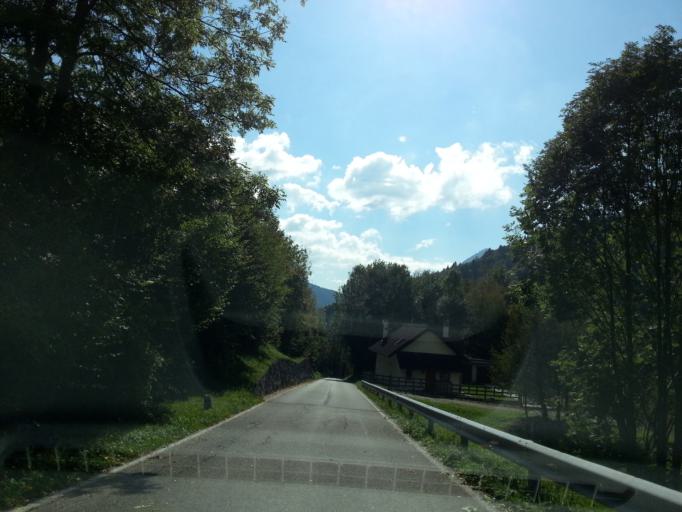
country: IT
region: Friuli Venezia Giulia
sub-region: Provincia di Udine
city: Pontebba
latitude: 46.5157
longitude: 13.2988
